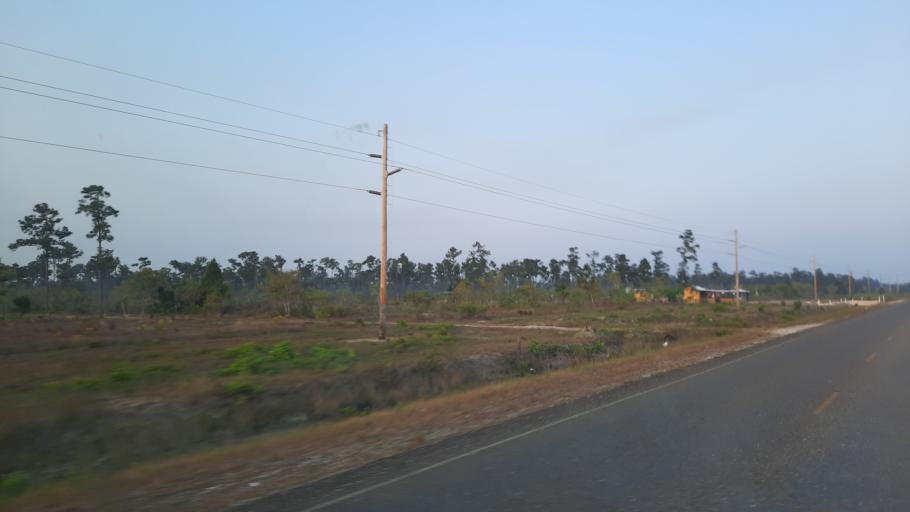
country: BZ
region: Stann Creek
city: Placencia
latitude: 16.5317
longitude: -88.4619
